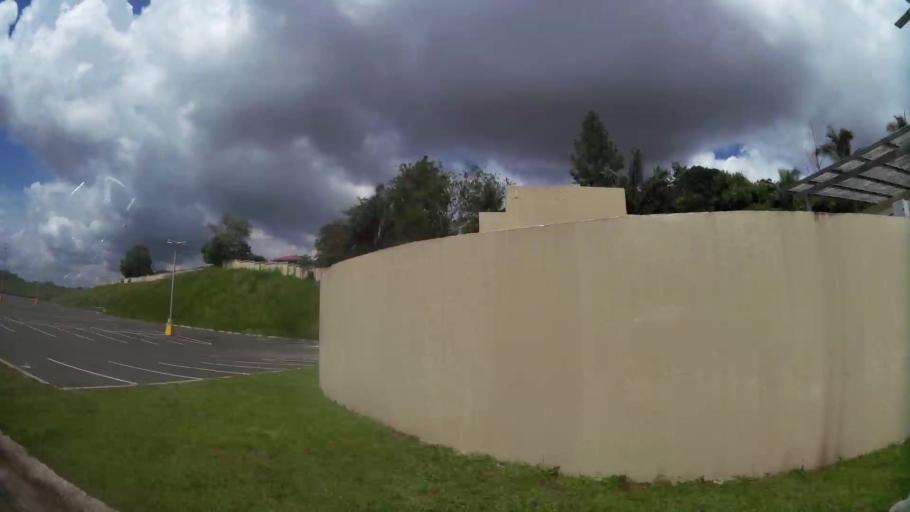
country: PA
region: Panama
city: Vista Alegre
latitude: 8.9235
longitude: -79.7057
